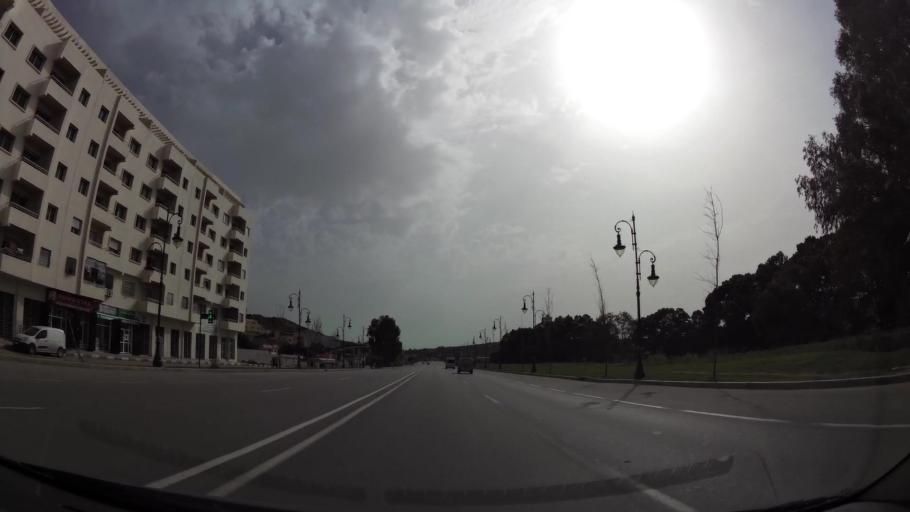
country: MA
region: Tanger-Tetouan
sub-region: Tanger-Assilah
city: Boukhalef
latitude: 35.7029
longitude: -5.9126
